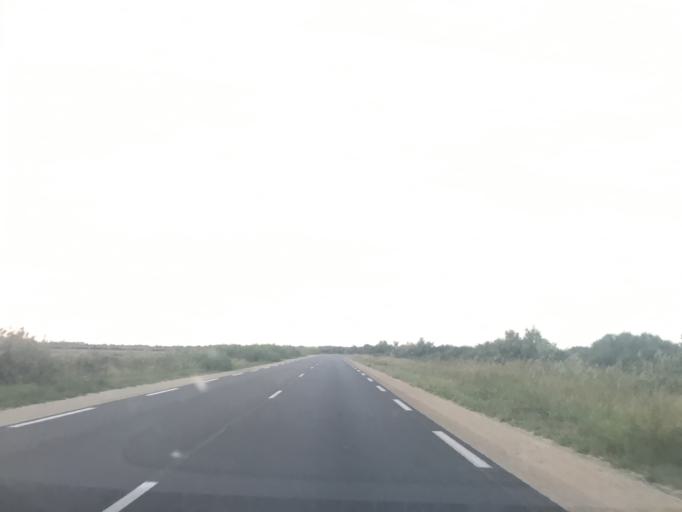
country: FR
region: Provence-Alpes-Cote d'Azur
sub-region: Departement des Bouches-du-Rhone
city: Saintes-Maries-de-la-Mer
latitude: 43.5364
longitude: 4.4004
